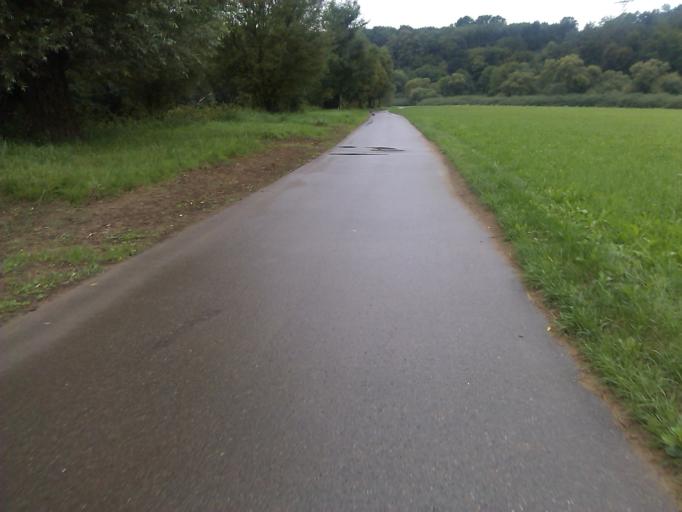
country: DE
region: Baden-Wuerttemberg
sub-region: Tuebingen Region
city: Pliezhausen
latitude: 48.5549
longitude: 9.1947
